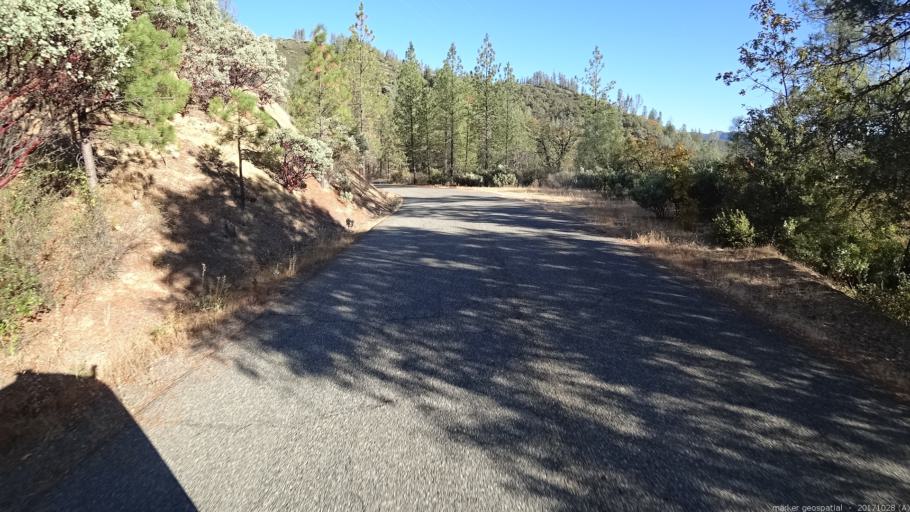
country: US
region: California
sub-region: Trinity County
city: Lewiston
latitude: 40.6626
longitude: -122.6593
